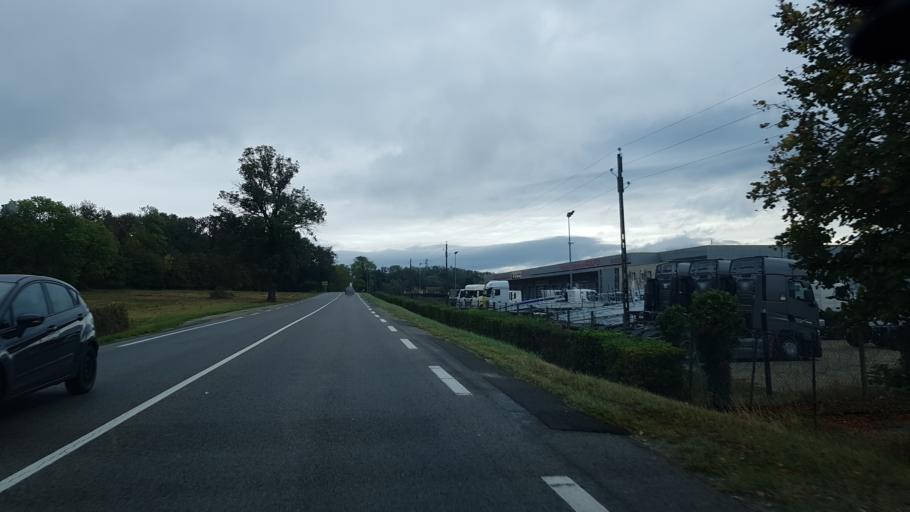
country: FR
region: Rhone-Alpes
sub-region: Departement de l'Ain
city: Saint-Martin-du-Mont
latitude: 46.0919
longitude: 5.3139
